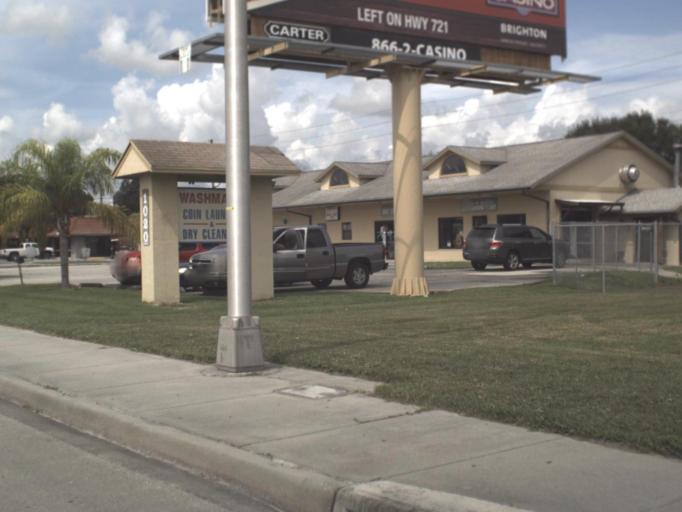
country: US
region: Florida
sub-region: Okeechobee County
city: Okeechobee
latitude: 27.2438
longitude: -80.8423
